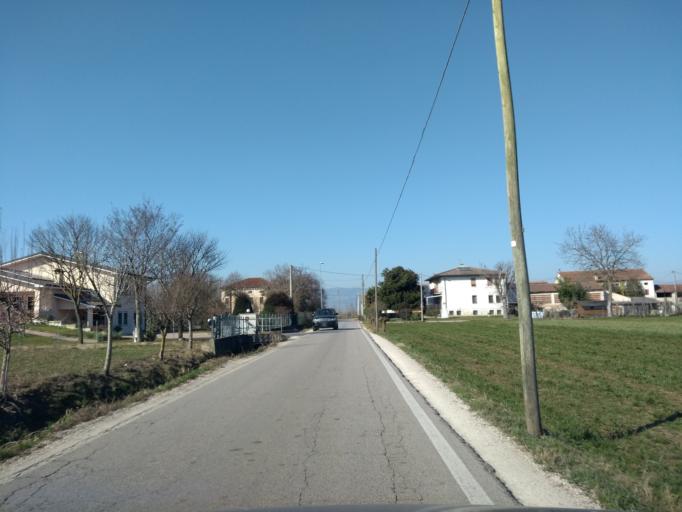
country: IT
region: Veneto
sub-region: Provincia di Padova
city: San Pietro in Gu
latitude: 45.6124
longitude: 11.6495
